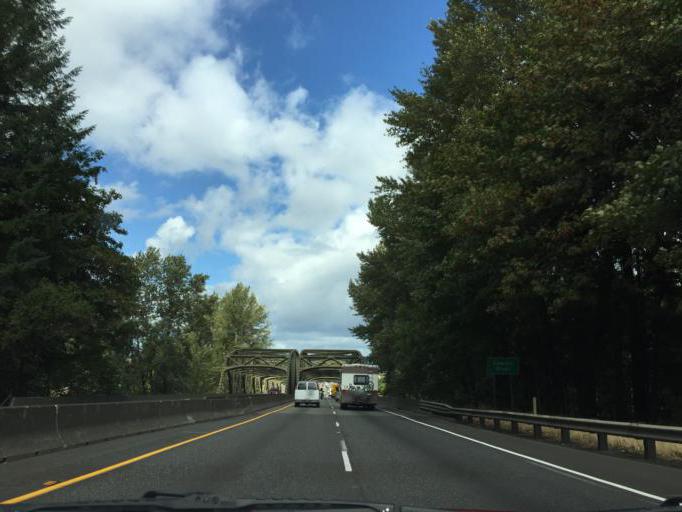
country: US
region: Washington
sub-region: Lewis County
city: Winlock
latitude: 46.4124
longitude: -122.8898
